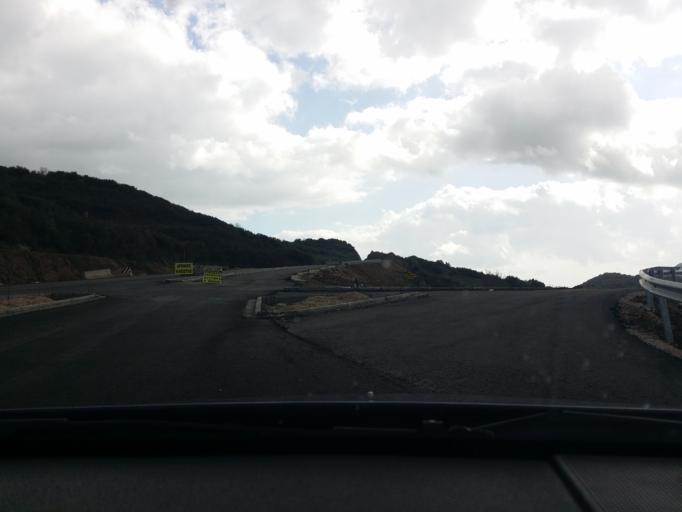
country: GR
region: West Greece
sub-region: Nomos Aitolias kai Akarnanias
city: Fitiai
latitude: 38.6857
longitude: 21.1847
